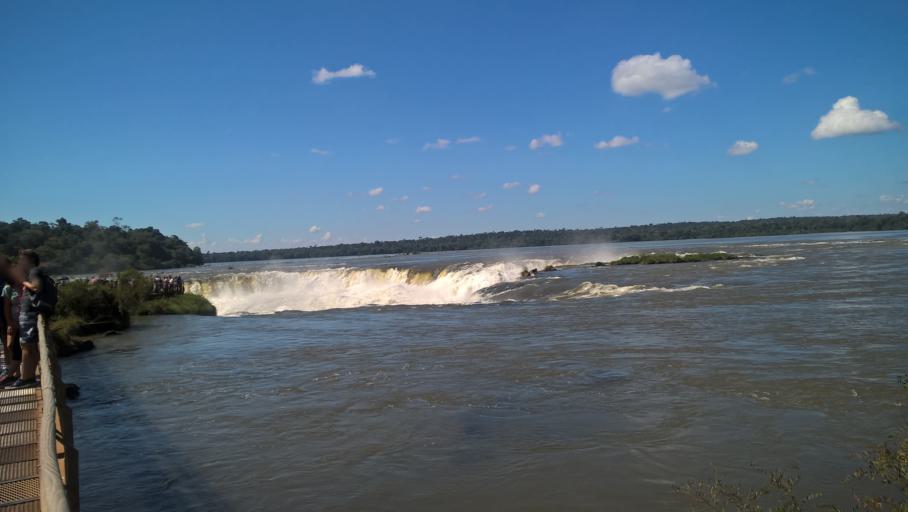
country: AR
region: Misiones
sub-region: Departamento de Iguazu
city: Puerto Iguazu
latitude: -25.6961
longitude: -54.4380
